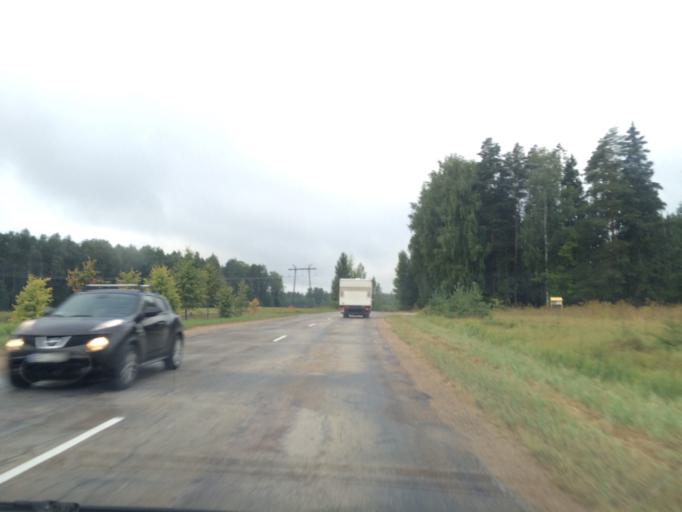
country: LV
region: Ikskile
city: Ikskile
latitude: 56.8604
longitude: 24.5522
